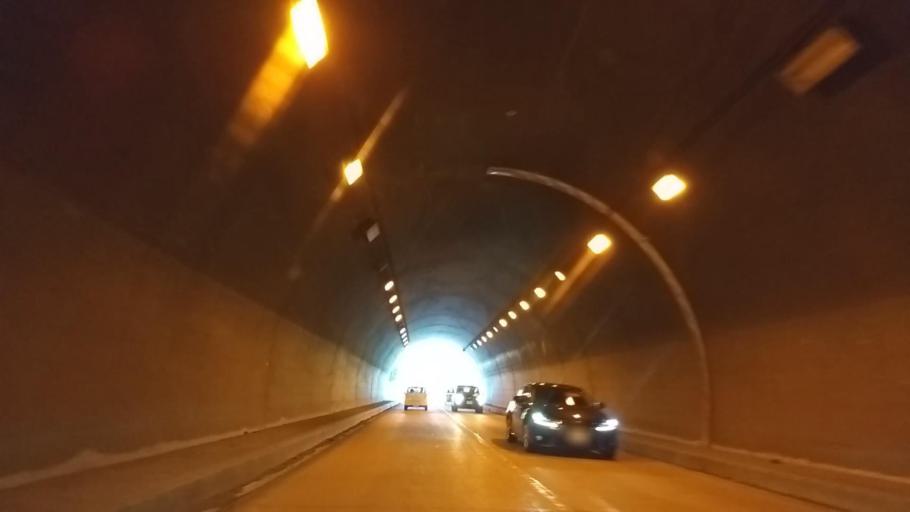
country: JP
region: Nagano
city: Komoro
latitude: 36.3440
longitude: 138.4403
